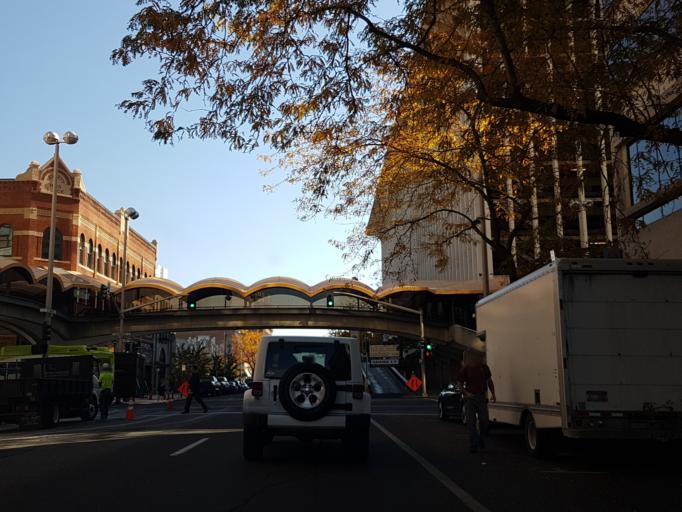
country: US
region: Washington
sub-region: Spokane County
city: Spokane
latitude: 47.6591
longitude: -117.4218
